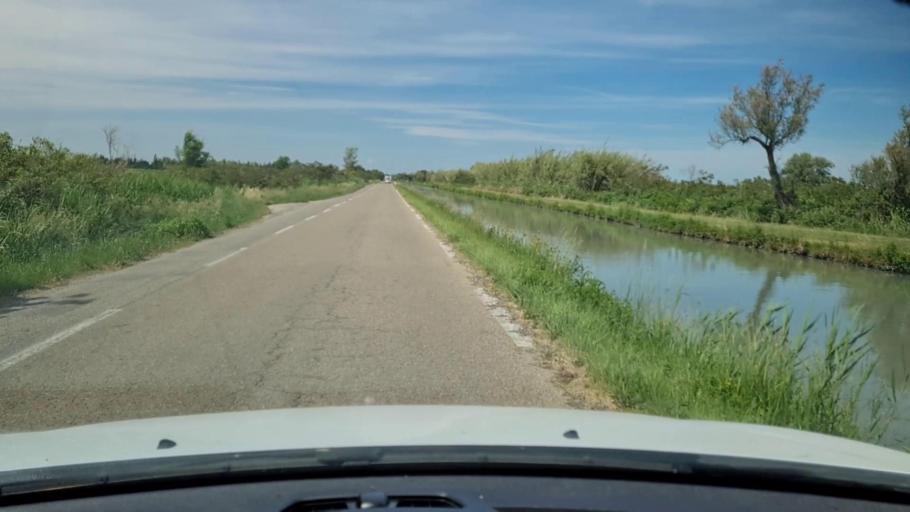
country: FR
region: Languedoc-Roussillon
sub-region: Departement du Gard
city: Vauvert
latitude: 43.5940
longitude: 4.3423
